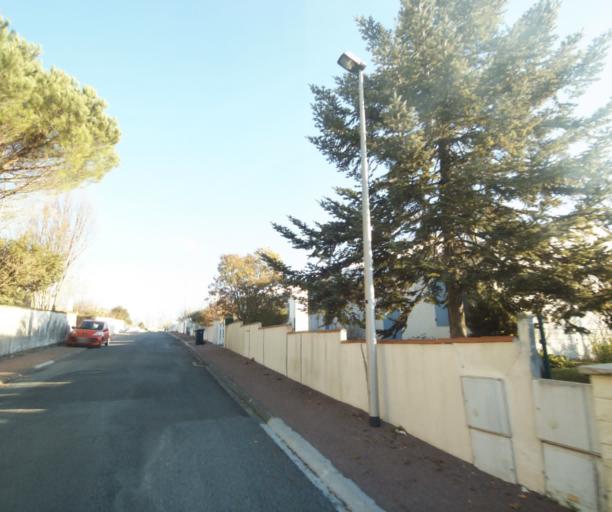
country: FR
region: Poitou-Charentes
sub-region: Departement de la Charente-Maritime
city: Saintes
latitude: 45.7638
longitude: -0.6141
